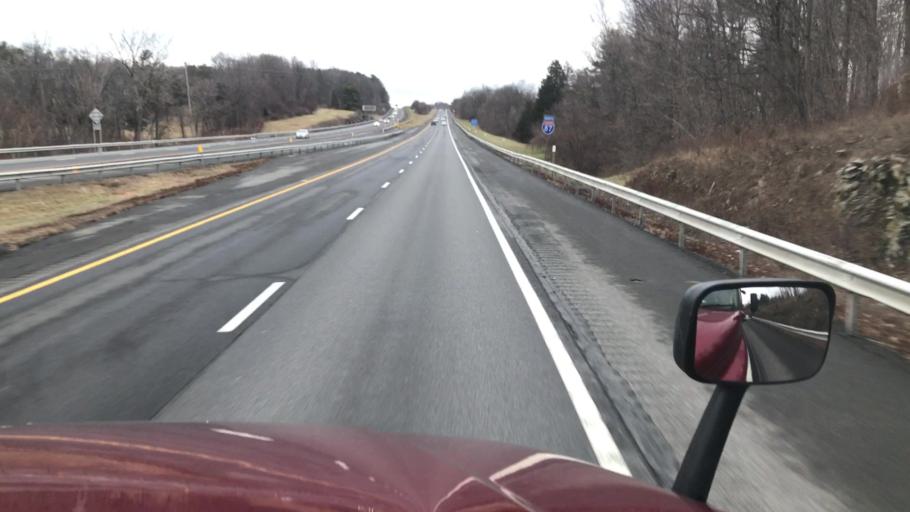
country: US
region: New York
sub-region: Greene County
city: Jefferson Heights
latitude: 42.2560
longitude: -73.8796
